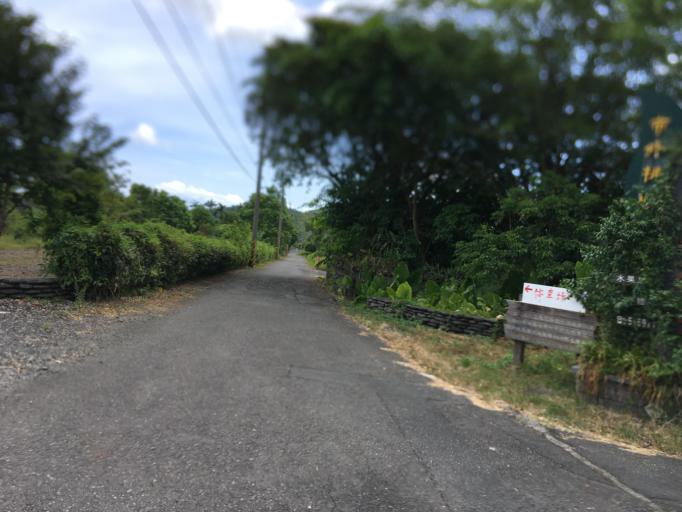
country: TW
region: Taiwan
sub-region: Yilan
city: Yilan
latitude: 24.6323
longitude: 121.7140
